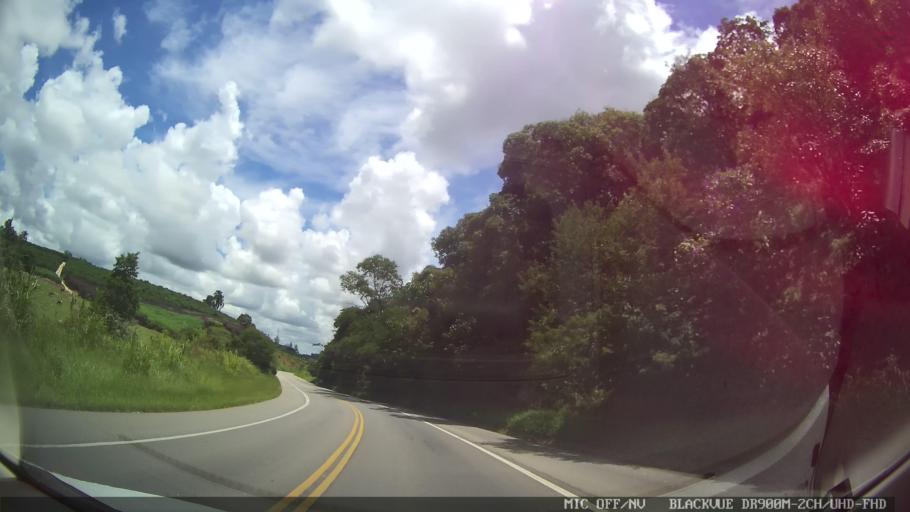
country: BR
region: Sao Paulo
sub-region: Amparo
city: Amparo
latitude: -22.7700
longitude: -46.7379
